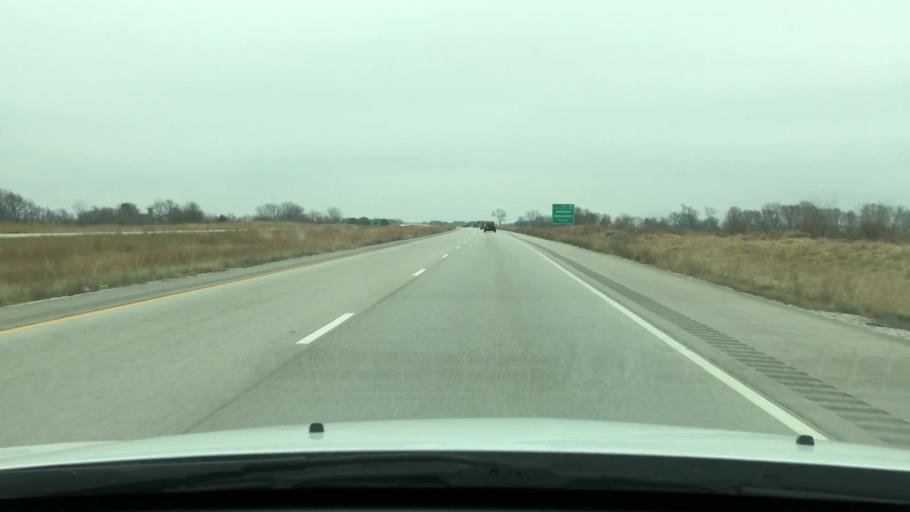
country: US
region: Illinois
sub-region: Morgan County
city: Jacksonville
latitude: 39.7370
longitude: -90.0702
